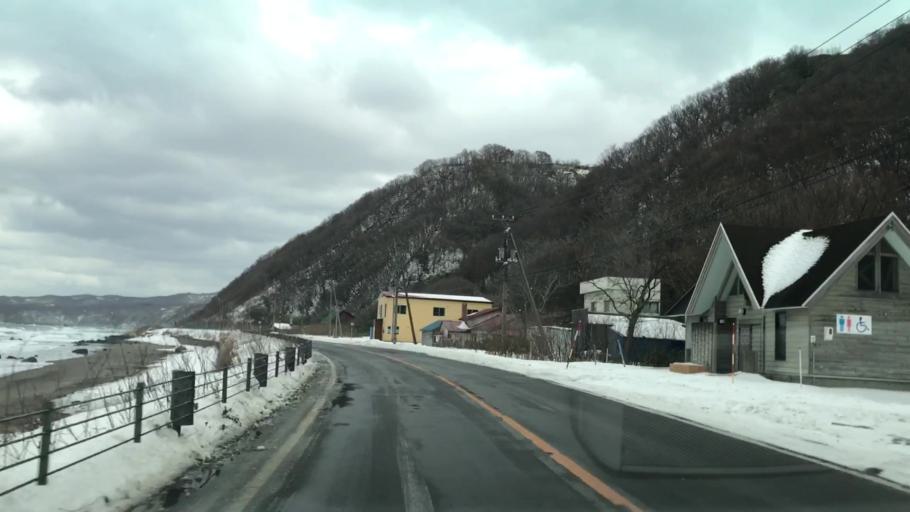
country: JP
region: Hokkaido
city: Iwanai
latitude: 43.3285
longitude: 140.4278
